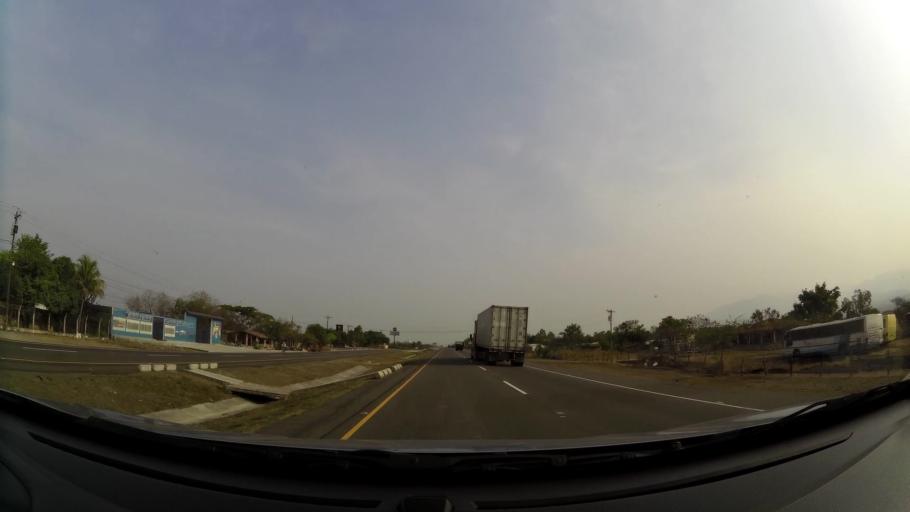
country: HN
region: Comayagua
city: Villa de San Antonio
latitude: 14.3309
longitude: -87.5882
